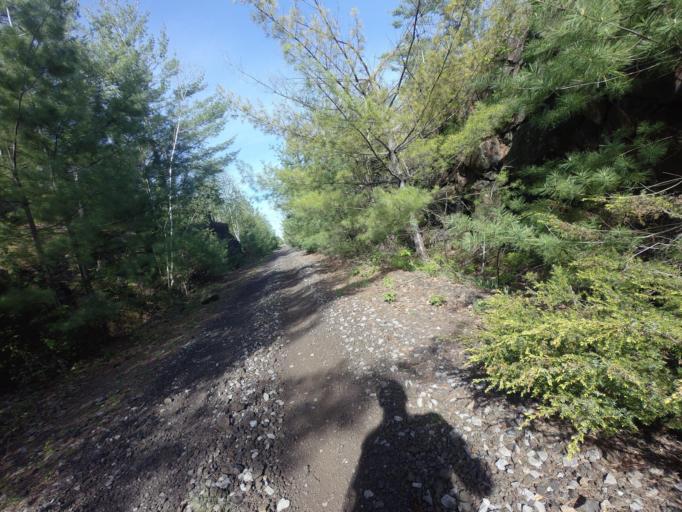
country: CA
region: Ontario
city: Arnprior
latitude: 45.4710
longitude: -76.2969
